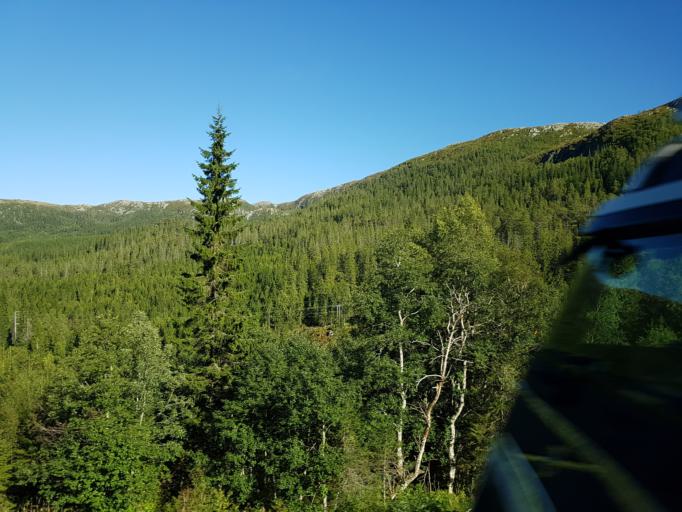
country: NO
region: Sor-Trondelag
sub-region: Afjord
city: A i Afjord
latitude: 63.7188
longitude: 10.2327
